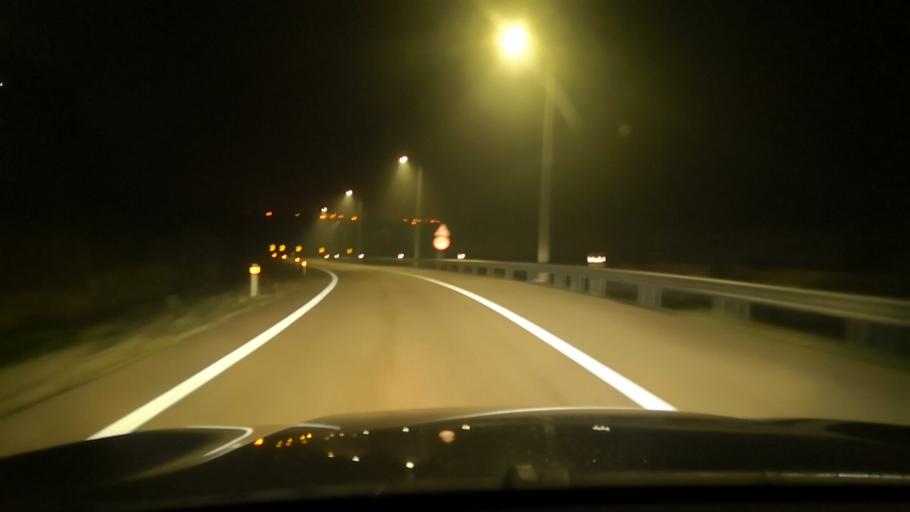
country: PT
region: Evora
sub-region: Vendas Novas
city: Vendas Novas
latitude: 38.6055
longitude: -8.6497
